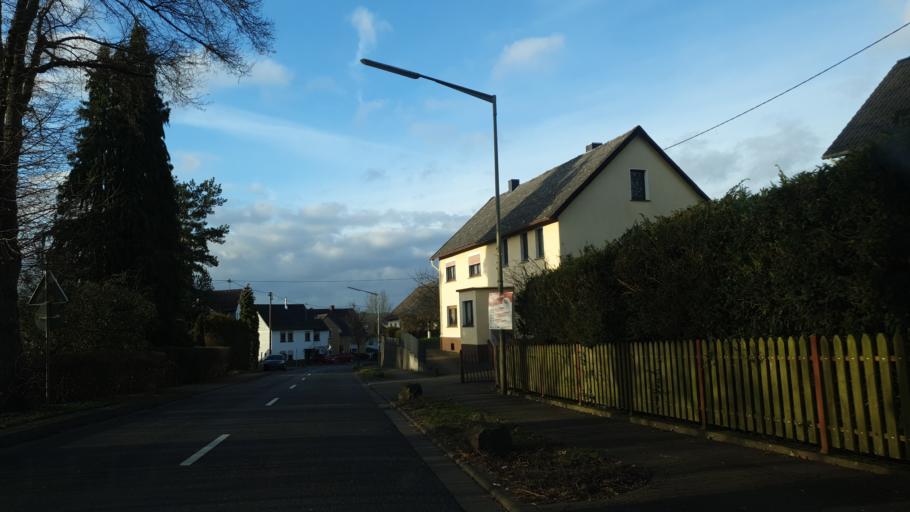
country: DE
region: Rheinland-Pfalz
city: Fluterschen
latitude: 50.6665
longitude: 7.6255
